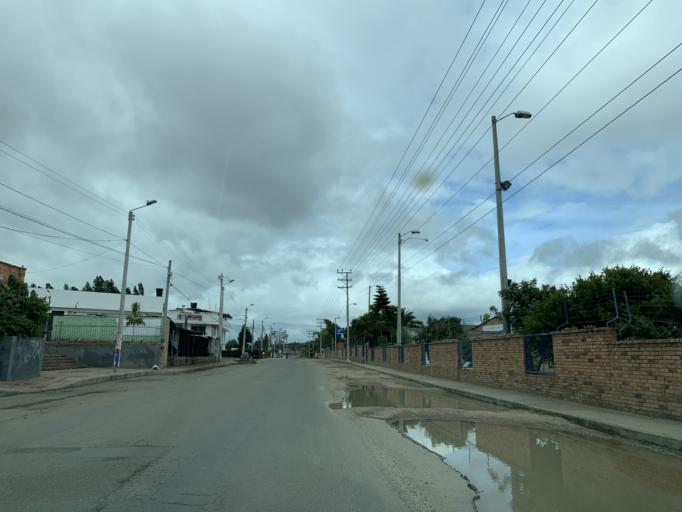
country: CO
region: Boyaca
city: Tunja
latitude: 5.5626
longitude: -73.3457
